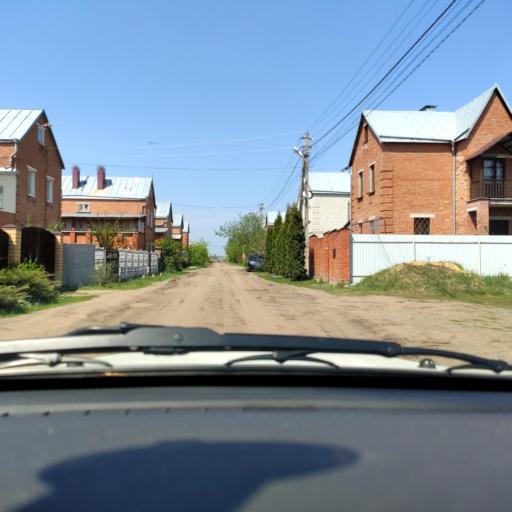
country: RU
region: Voronezj
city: Shilovo
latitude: 51.5629
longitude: 39.0640
